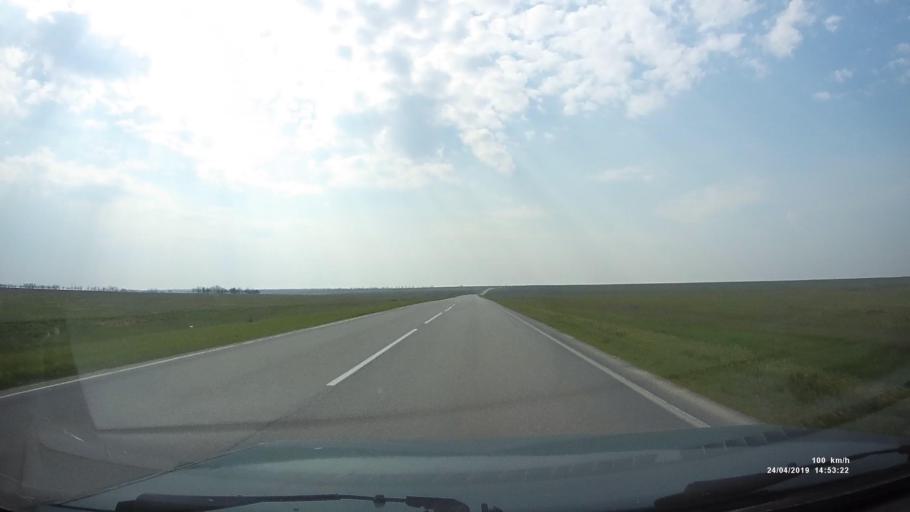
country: RU
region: Rostov
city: Remontnoye
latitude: 46.5312
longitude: 43.6606
